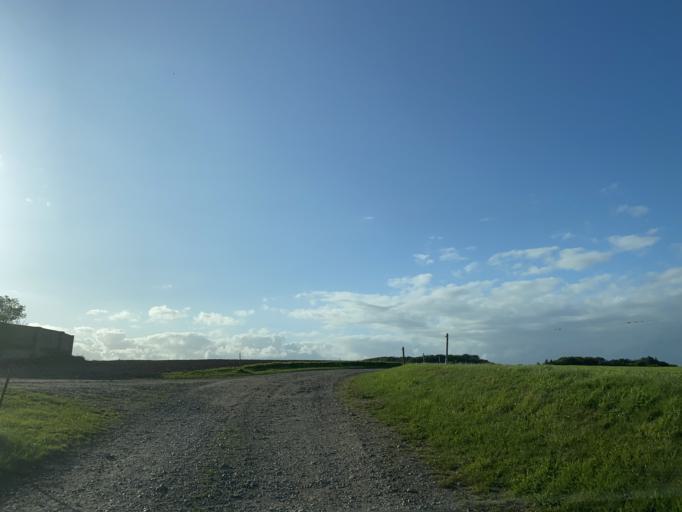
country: DK
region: Central Jutland
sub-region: Skanderborg Kommune
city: Ry
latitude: 56.1572
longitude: 9.8067
